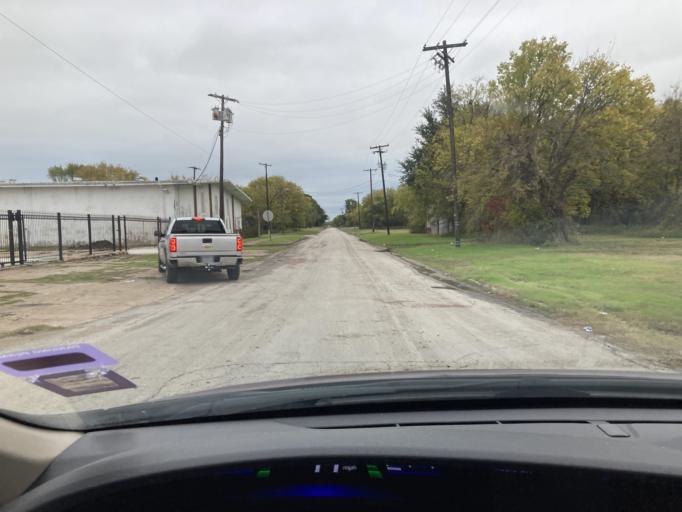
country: US
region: Texas
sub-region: Navarro County
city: Corsicana
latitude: 32.0920
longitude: -96.4605
